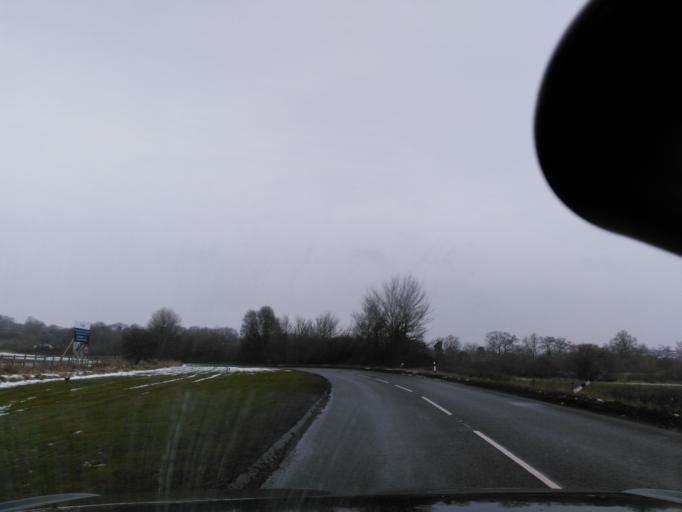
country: GB
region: England
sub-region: Wiltshire
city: Chippenham
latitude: 51.4400
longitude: -2.1318
